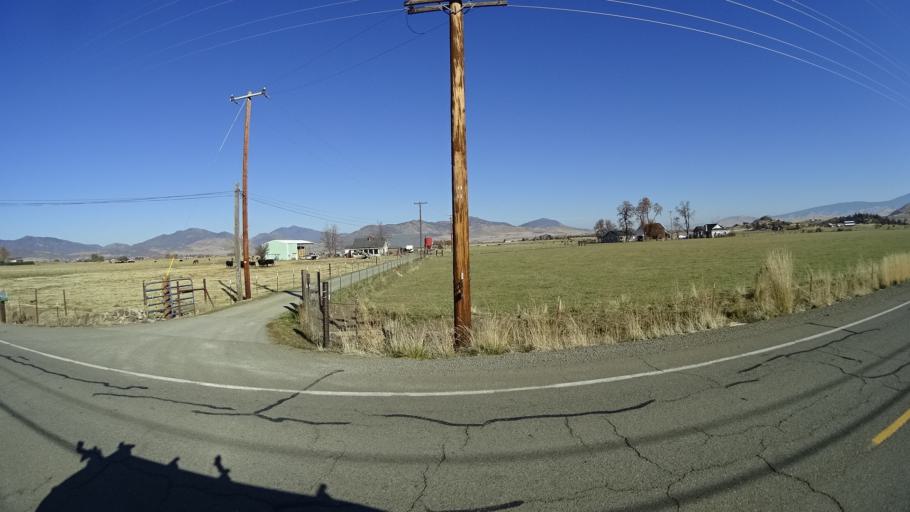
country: US
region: California
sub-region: Siskiyou County
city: Montague
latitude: 41.7056
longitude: -122.5524
